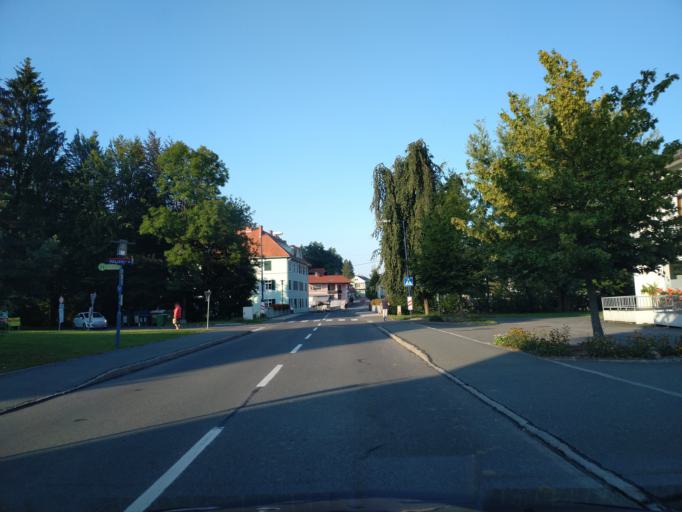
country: AT
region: Styria
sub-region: Politischer Bezirk Deutschlandsberg
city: Wies
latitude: 46.7164
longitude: 15.2654
